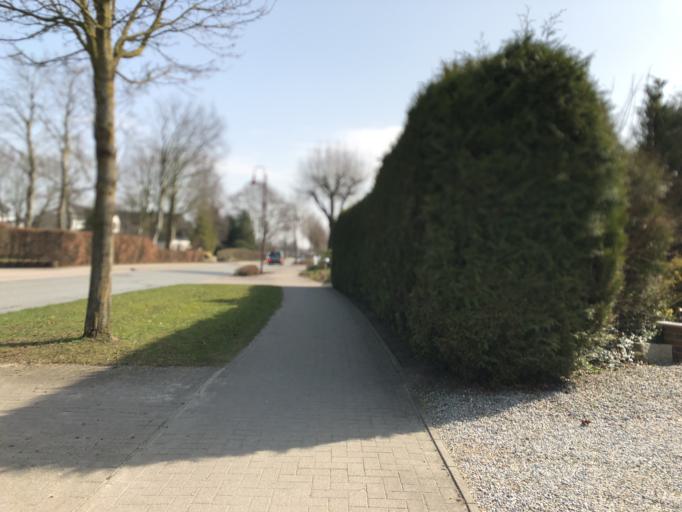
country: DE
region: Schleswig-Holstein
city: Tarp
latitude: 54.6700
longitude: 9.3897
